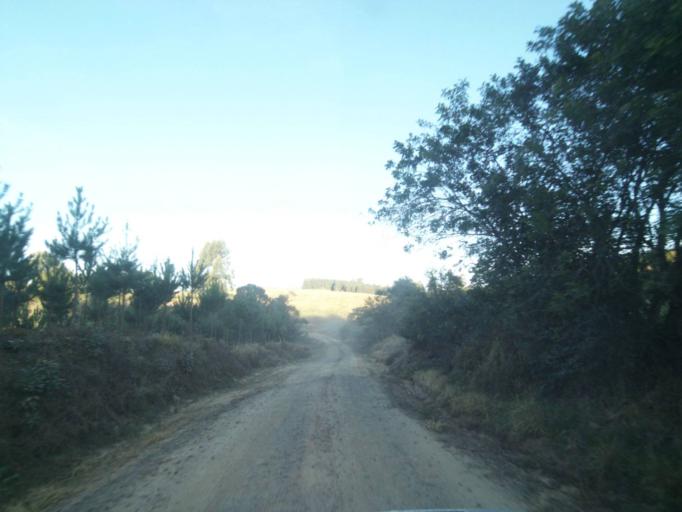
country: BR
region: Parana
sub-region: Tibagi
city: Tibagi
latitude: -24.5400
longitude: -50.6037
